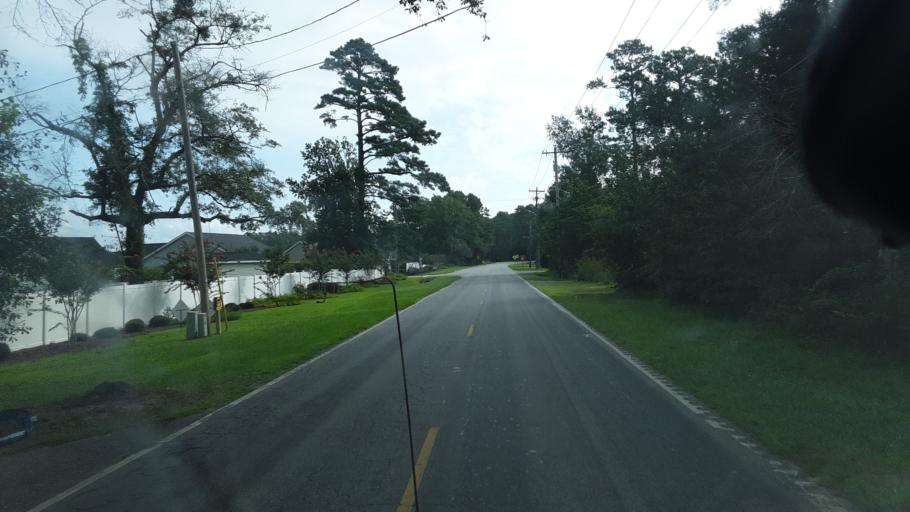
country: US
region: South Carolina
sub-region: Horry County
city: Conway
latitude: 33.8213
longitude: -79.0839
